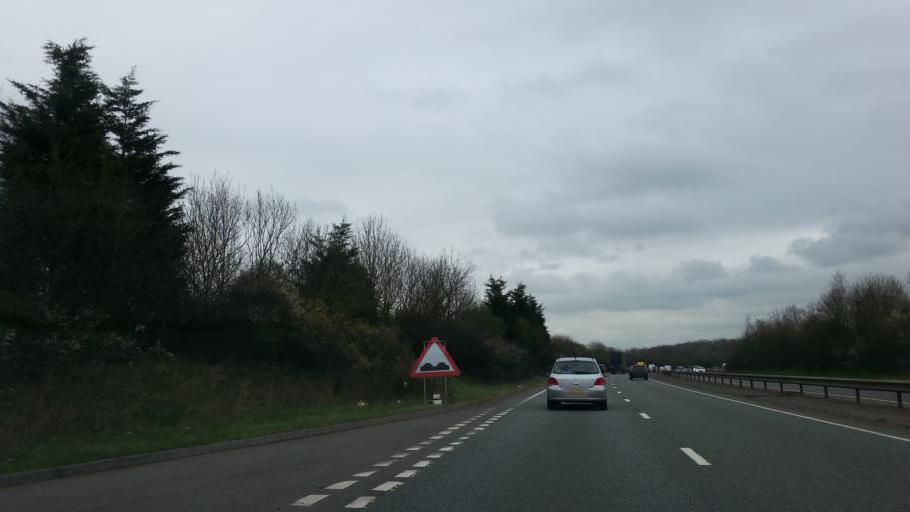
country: GB
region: England
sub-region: Leicestershire
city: Mountsorrel
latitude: 52.6871
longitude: -1.1587
